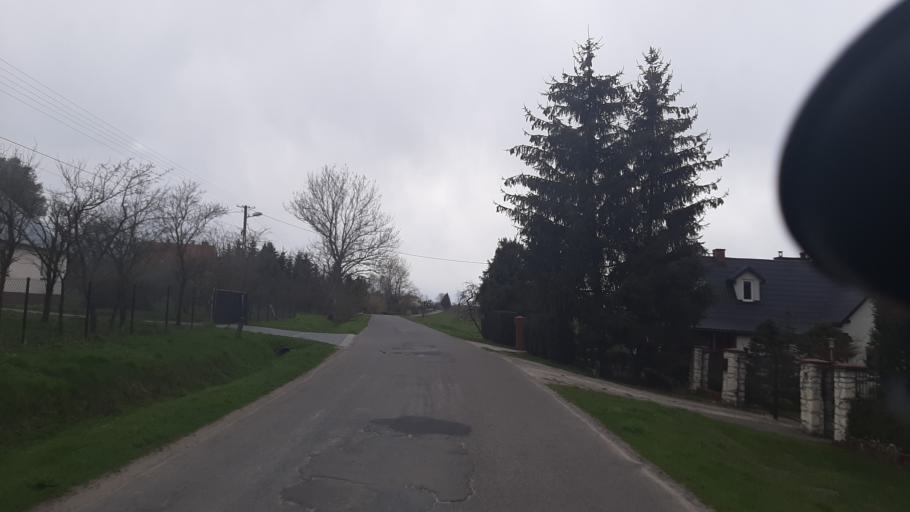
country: PL
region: Lublin Voivodeship
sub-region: Powiat lubelski
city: Niemce
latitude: 51.3651
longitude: 22.5431
